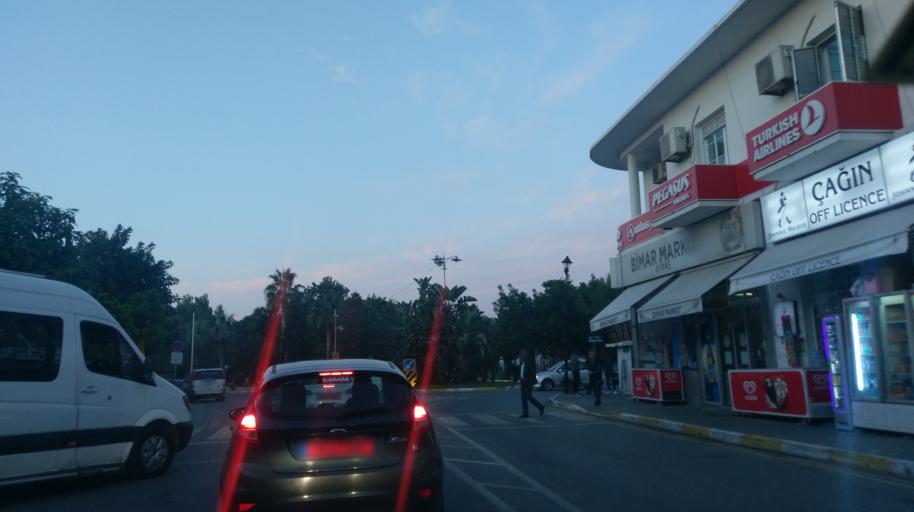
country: CY
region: Keryneia
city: Kyrenia
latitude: 35.3392
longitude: 33.3204
